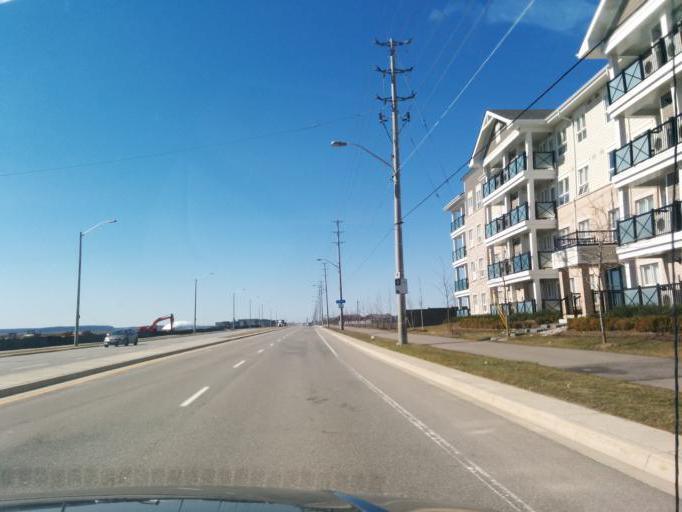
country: CA
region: Ontario
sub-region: Halton
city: Milton
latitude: 43.4959
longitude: -79.8490
